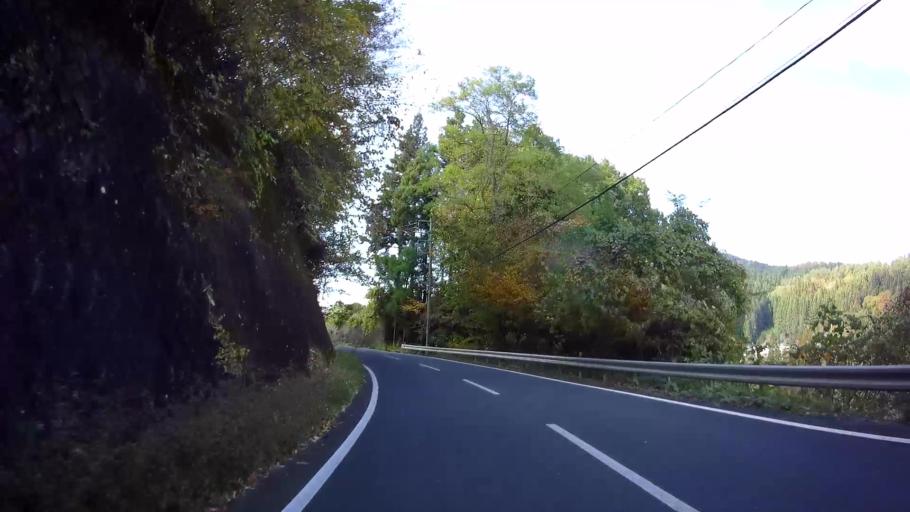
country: JP
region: Gunma
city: Nakanojomachi
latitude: 36.5057
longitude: 138.7314
